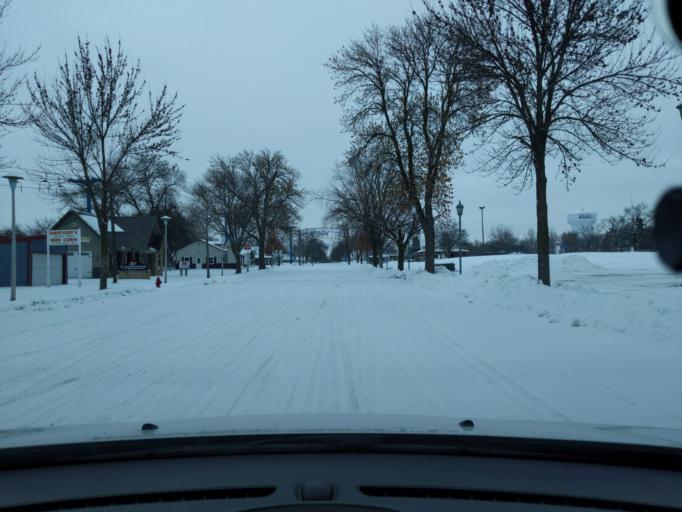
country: US
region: Minnesota
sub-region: Ramsey County
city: Falcon Heights
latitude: 44.9818
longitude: -93.1705
